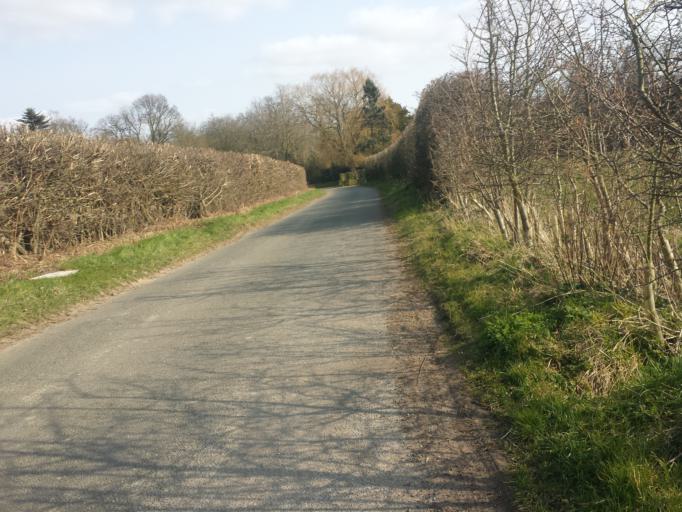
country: GB
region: England
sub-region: Essex
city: Little Clacton
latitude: 51.8976
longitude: 1.1568
